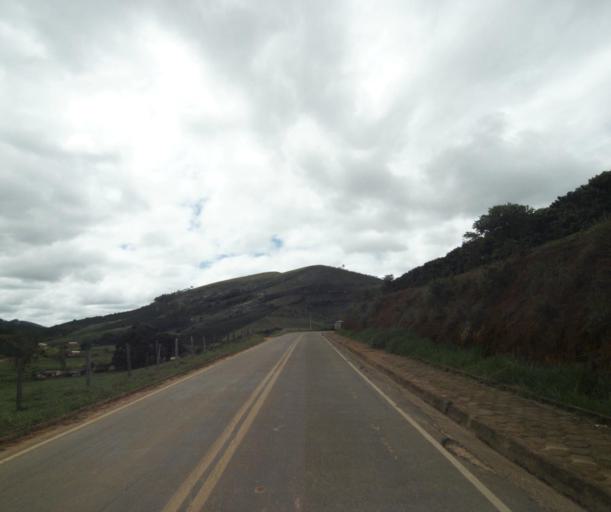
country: BR
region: Espirito Santo
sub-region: Irupi
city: Irupi
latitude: -20.3514
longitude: -41.6278
